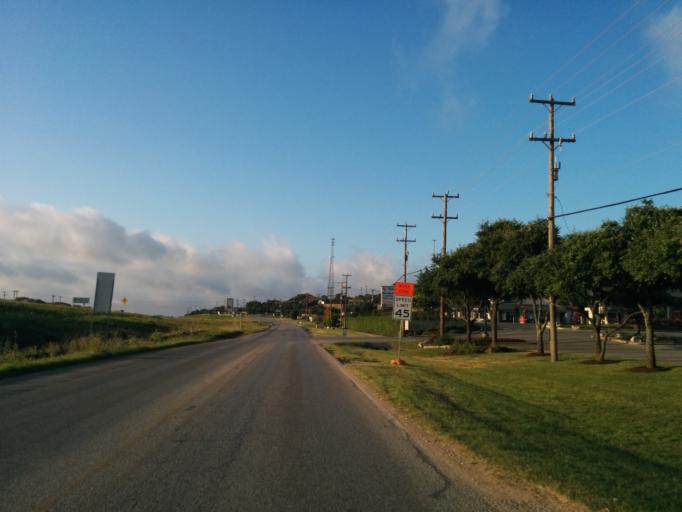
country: US
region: Texas
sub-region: Bexar County
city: Cross Mountain
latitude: 29.6657
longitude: -98.6320
